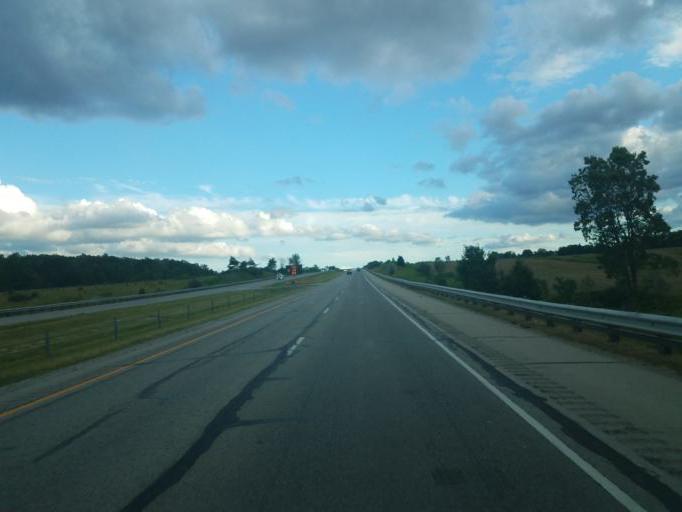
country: US
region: Indiana
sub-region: DeKalb County
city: Garrett
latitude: 41.2873
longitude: -85.0868
